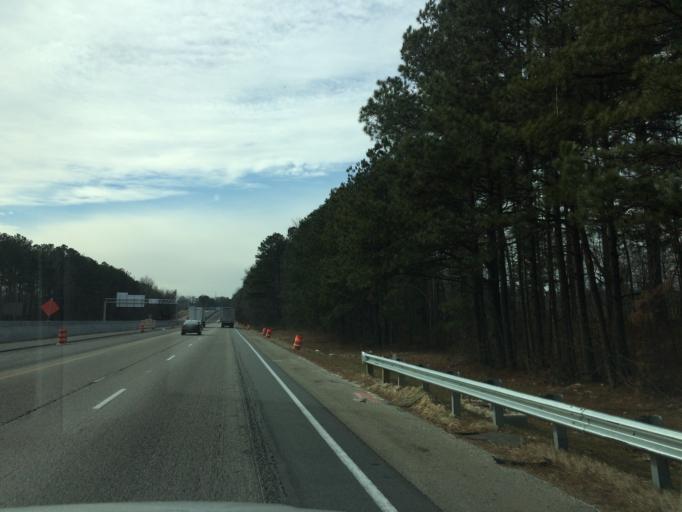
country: US
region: Georgia
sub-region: Gwinnett County
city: Buford
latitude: 34.0686
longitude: -83.9339
